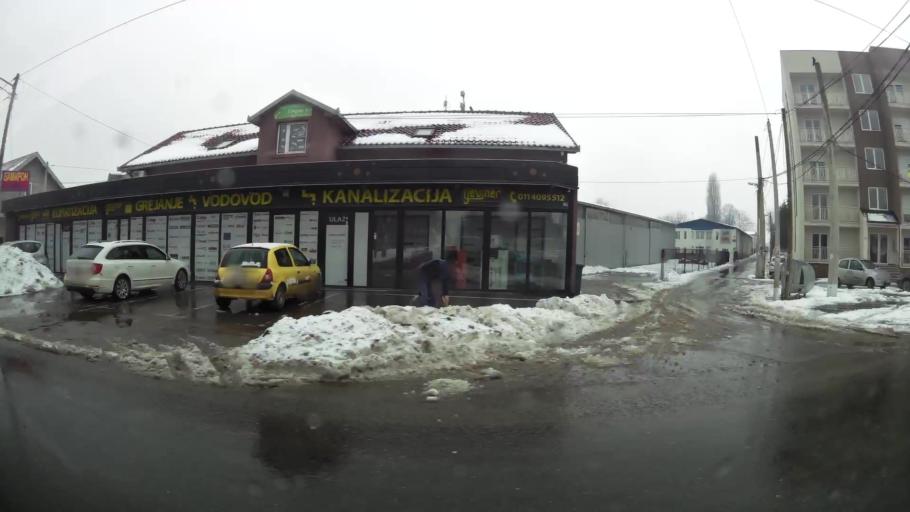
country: RS
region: Central Serbia
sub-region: Belgrade
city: Zemun
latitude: 44.8578
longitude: 20.3560
